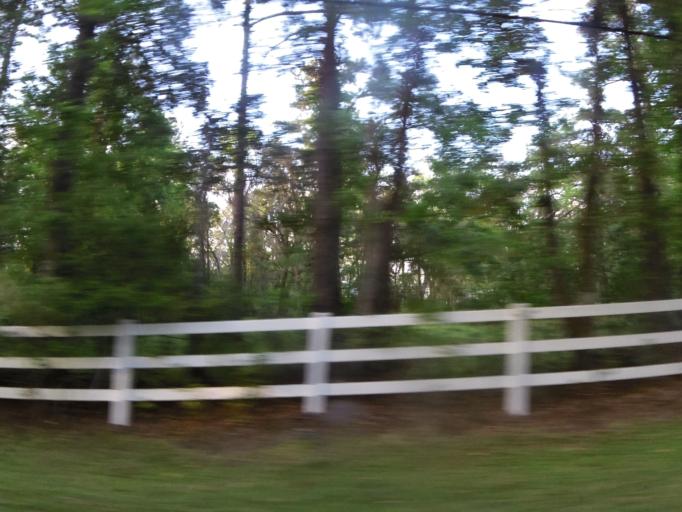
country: US
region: Florida
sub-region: Saint Johns County
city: Fruit Cove
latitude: 30.1270
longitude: -81.6064
